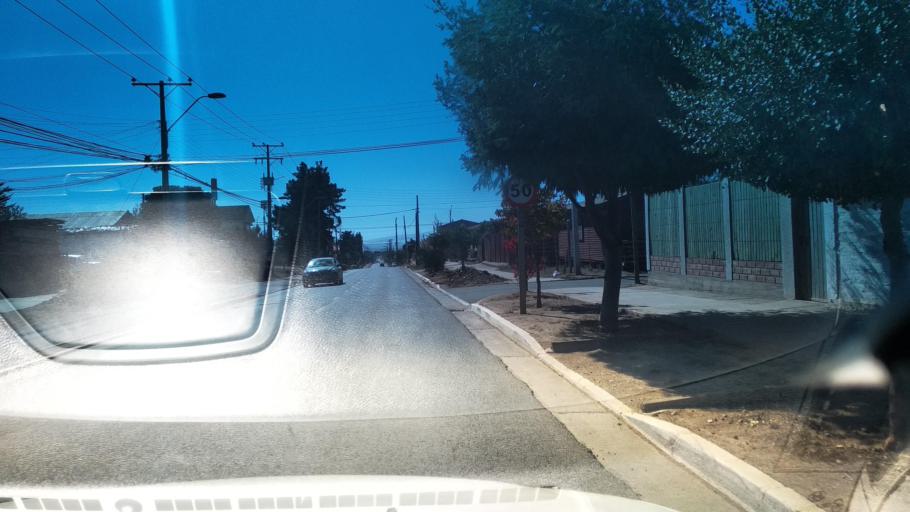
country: CL
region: O'Higgins
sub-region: Provincia de Colchagua
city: Santa Cruz
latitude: -34.4026
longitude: -71.9957
